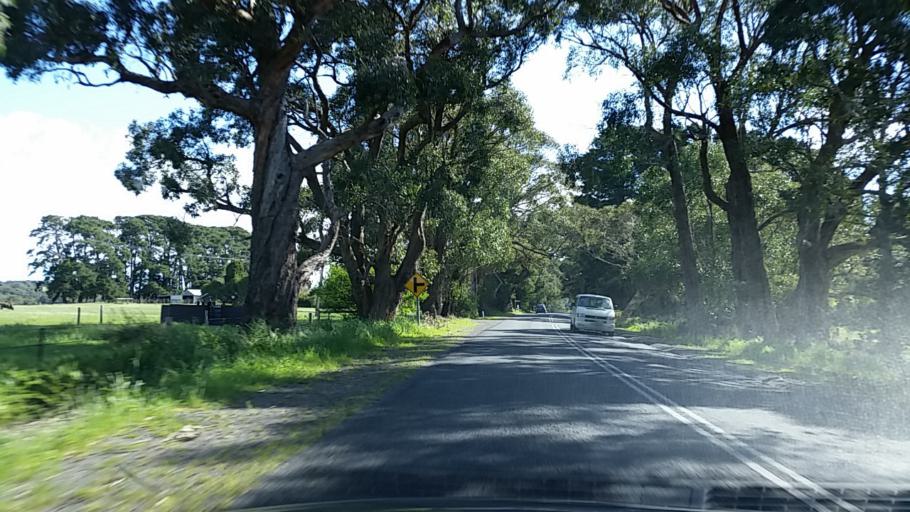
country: AU
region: South Australia
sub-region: Alexandrina
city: Mount Compass
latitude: -35.2659
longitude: 138.6445
